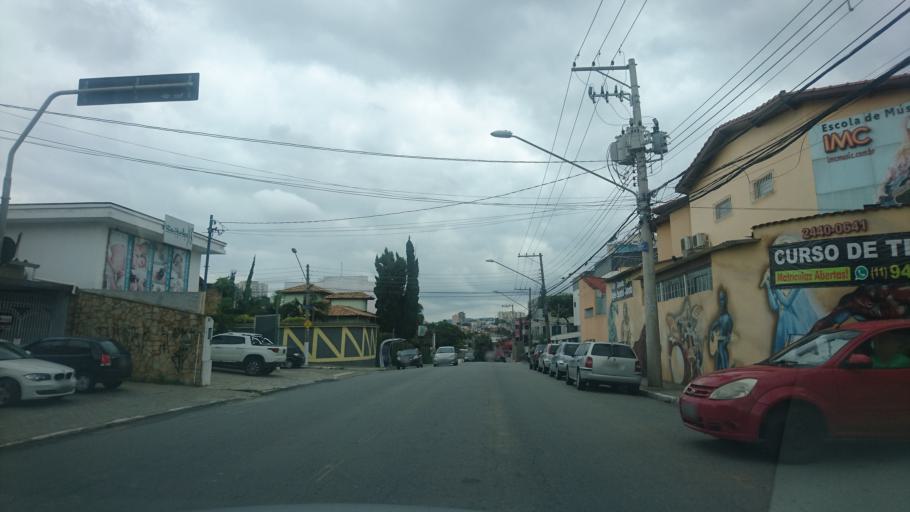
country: BR
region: Sao Paulo
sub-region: Guarulhos
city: Guarulhos
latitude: -23.4548
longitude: -46.5291
